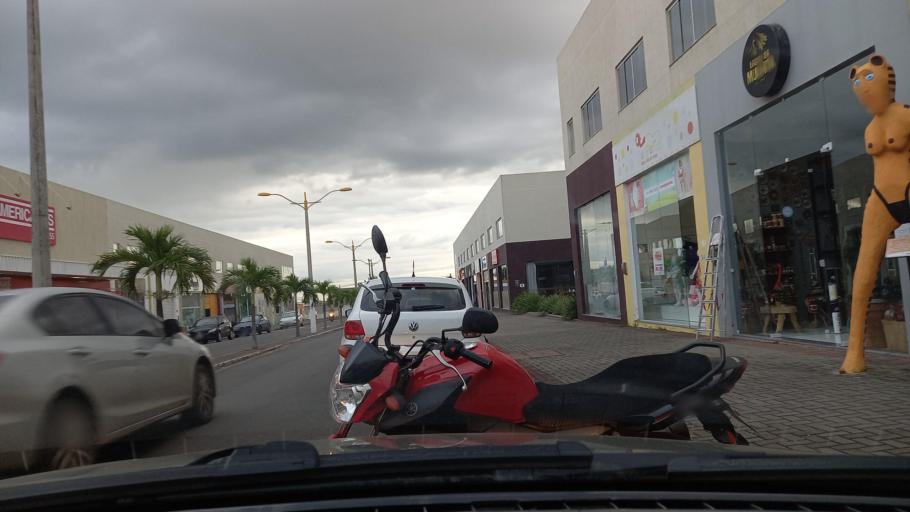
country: BR
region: Sergipe
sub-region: Caninde De Sao Francisco
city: Caninde de Sao Francisco
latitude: -9.6091
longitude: -37.7627
